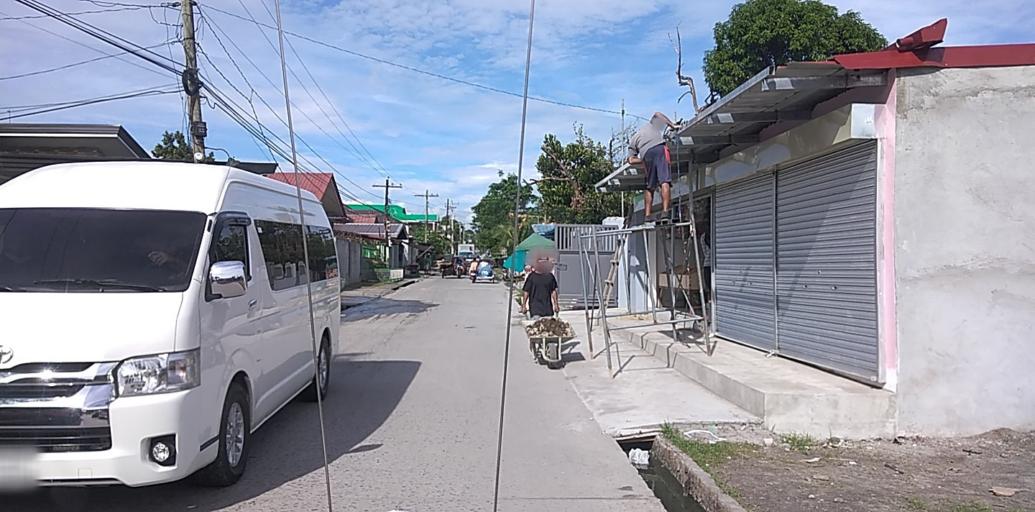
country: PH
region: Central Luzon
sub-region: Province of Pampanga
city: Angeles City
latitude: 15.1283
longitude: 120.5662
